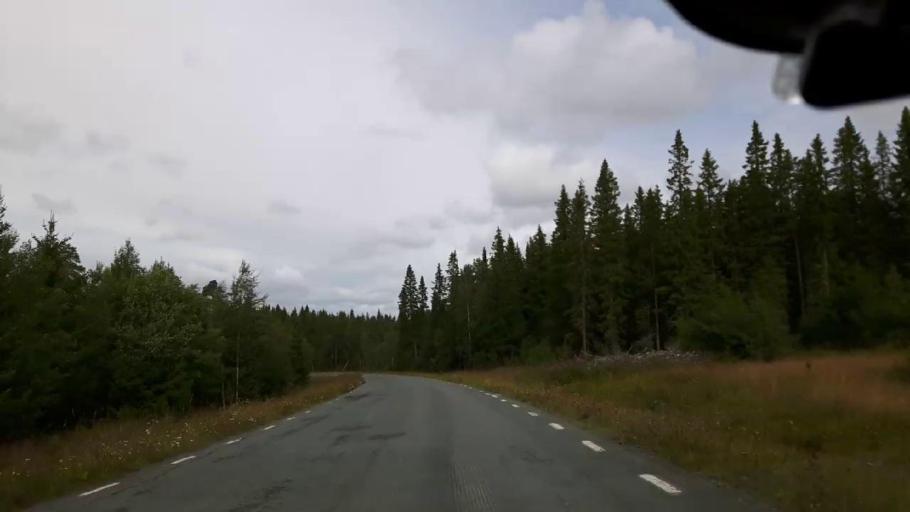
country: SE
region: Jaemtland
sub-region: Krokoms Kommun
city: Valla
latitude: 63.4573
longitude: 14.0423
